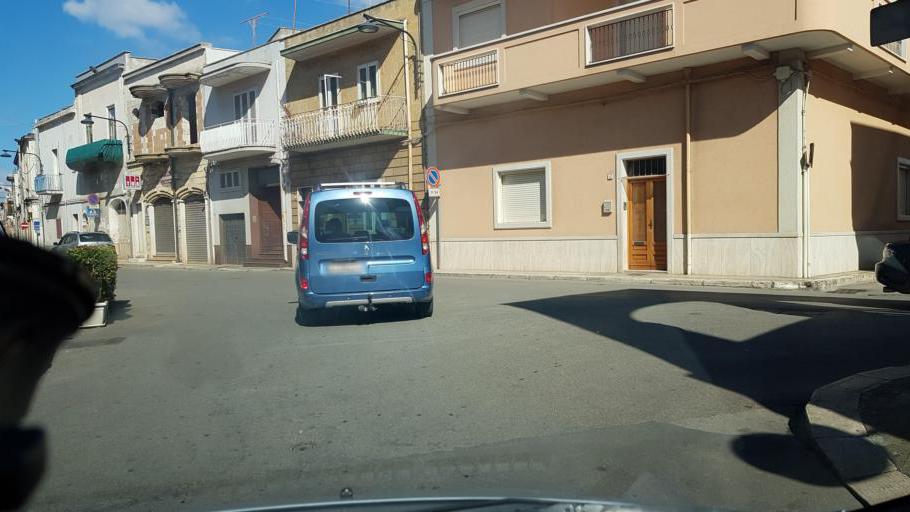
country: IT
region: Apulia
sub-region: Provincia di Brindisi
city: San Vito dei Normanni
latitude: 40.6561
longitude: 17.7078
